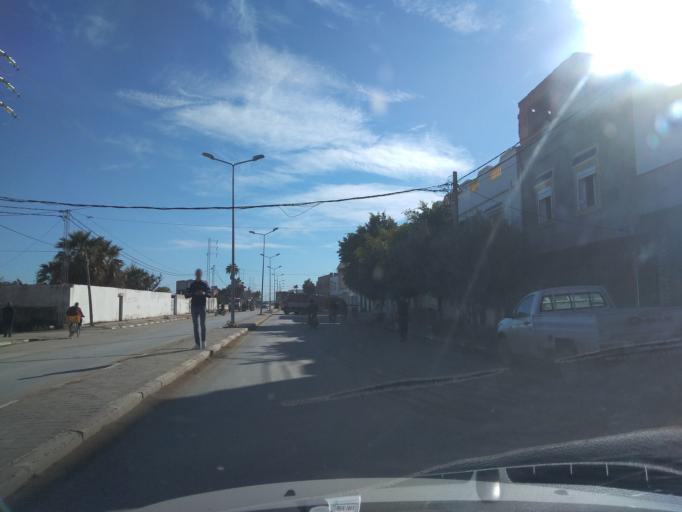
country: TN
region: Ariana
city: Qal'at al Andalus
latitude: 37.0577
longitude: 10.1201
